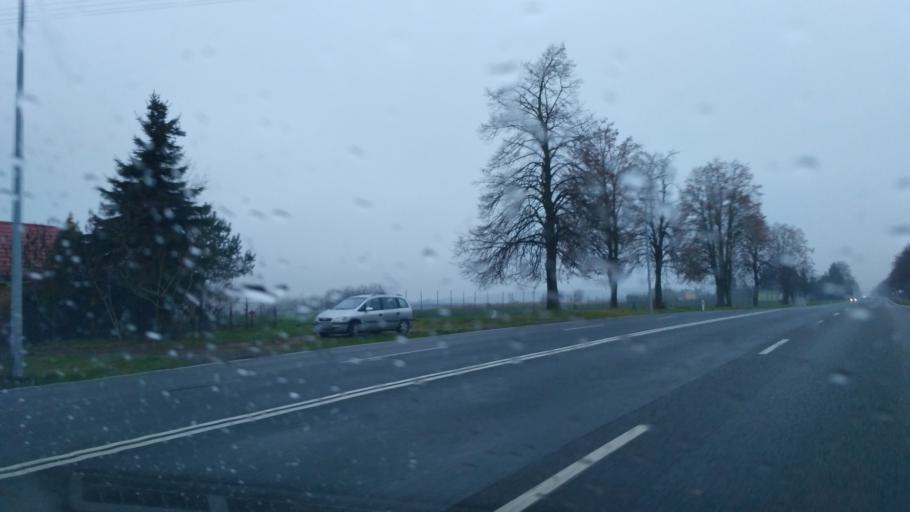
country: PL
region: Subcarpathian Voivodeship
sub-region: Powiat przeworski
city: Grzeska
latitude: 50.0625
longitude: 22.4561
